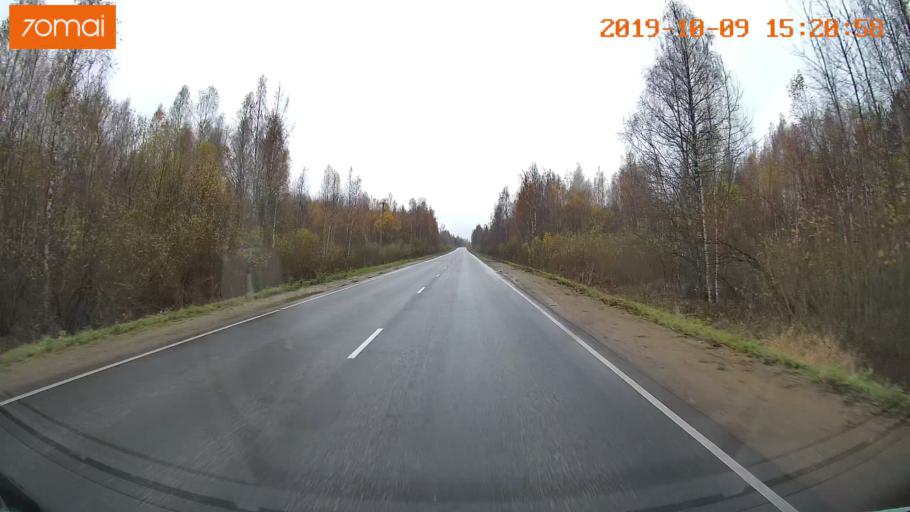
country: RU
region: Kostroma
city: Susanino
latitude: 58.0585
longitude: 41.5282
